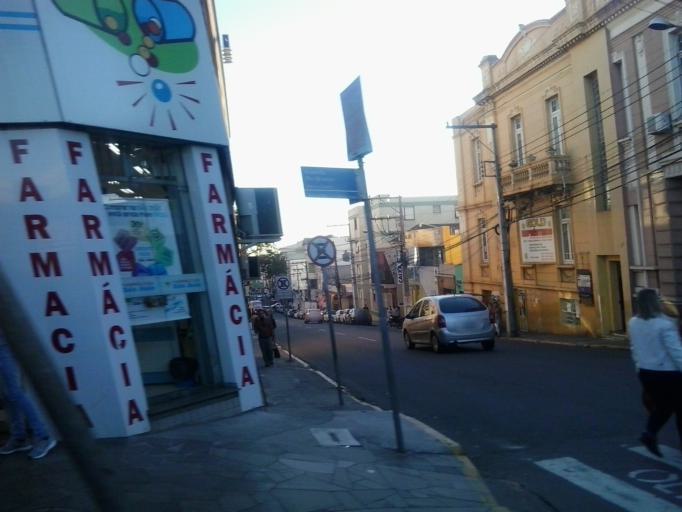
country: BR
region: Rio Grande do Sul
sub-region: Santa Maria
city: Santa Maria
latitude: -29.6844
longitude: -53.8080
